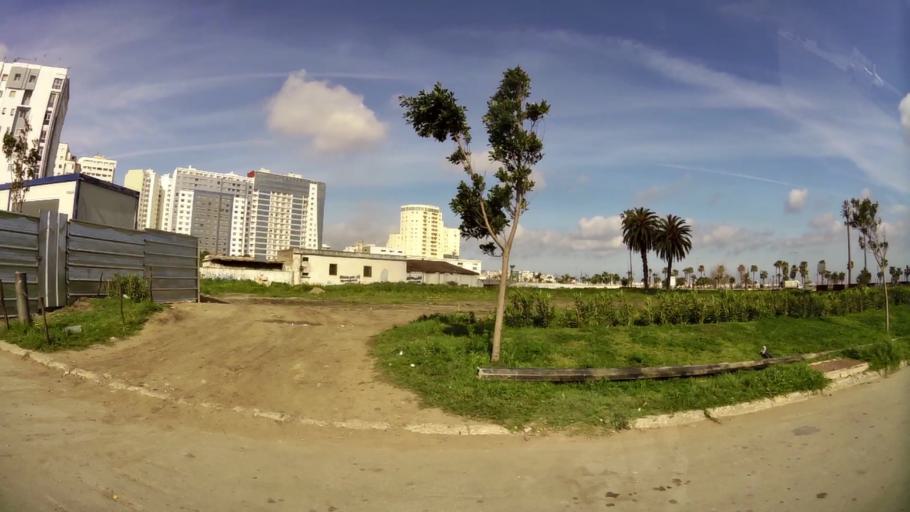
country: MA
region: Tanger-Tetouan
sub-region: Tanger-Assilah
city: Tangier
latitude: 35.7740
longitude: -5.7903
